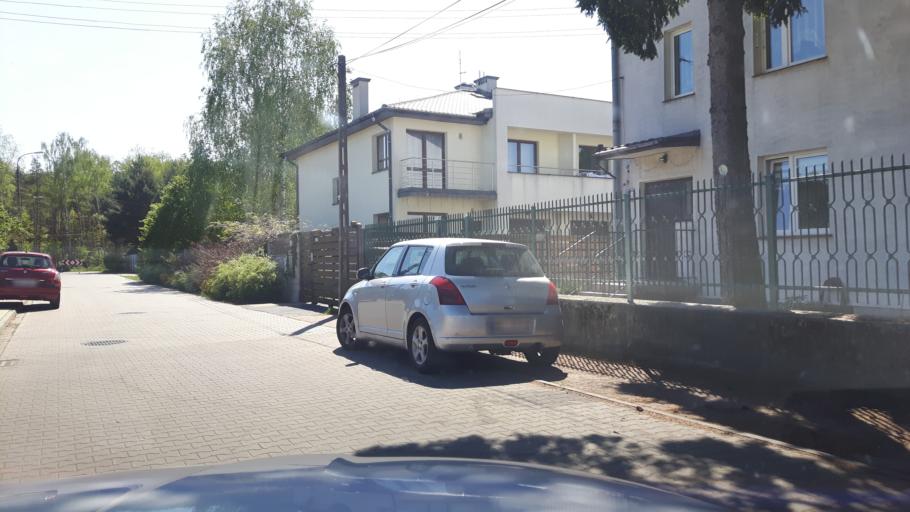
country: PL
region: Masovian Voivodeship
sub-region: Warszawa
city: Rembertow
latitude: 52.2480
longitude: 21.1722
